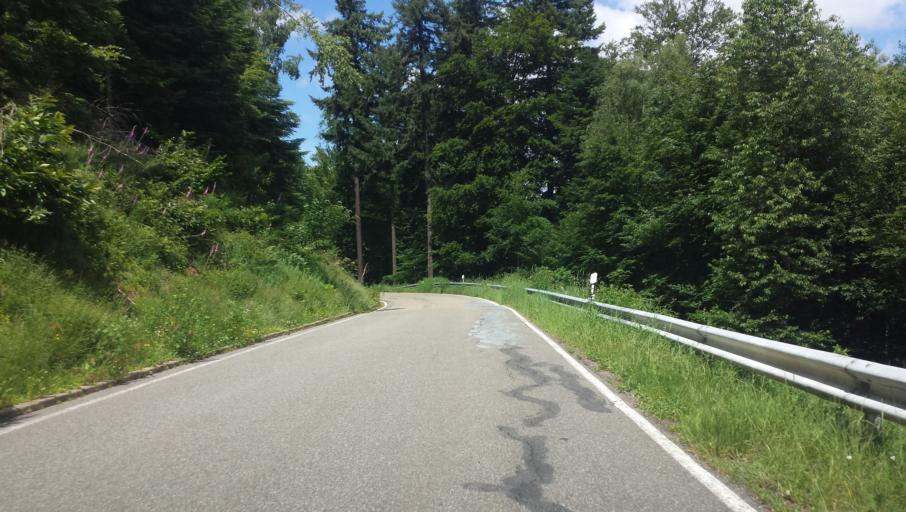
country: DE
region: Rheinland-Pfalz
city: Annweiler am Trifels
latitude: 49.1863
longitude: 7.9717
